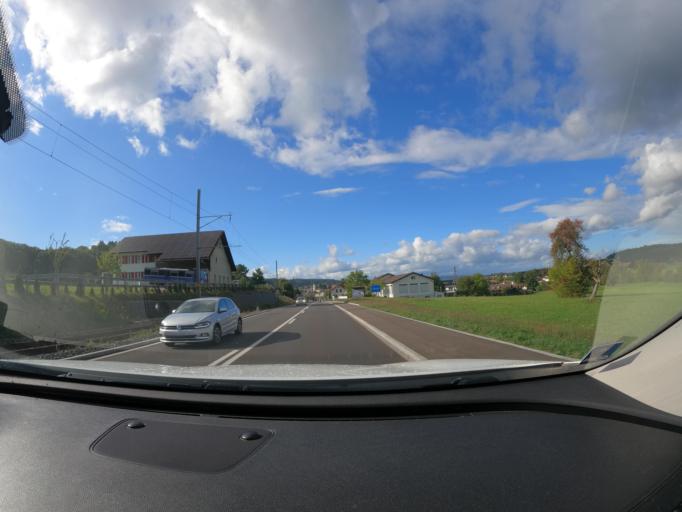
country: CH
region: Aargau
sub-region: Bezirk Lenzburg
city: Seon
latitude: 47.3388
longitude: 8.1654
